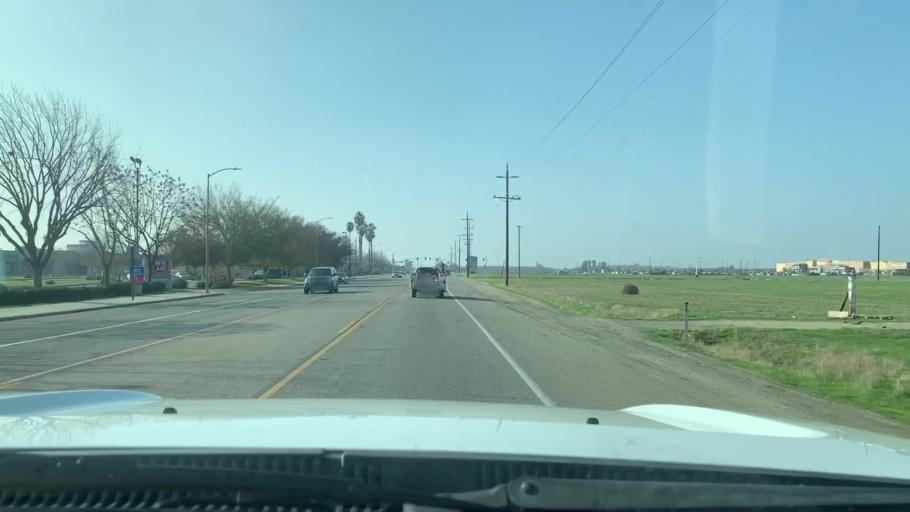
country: US
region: California
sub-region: Kern County
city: Wasco
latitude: 35.6016
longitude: -119.3539
